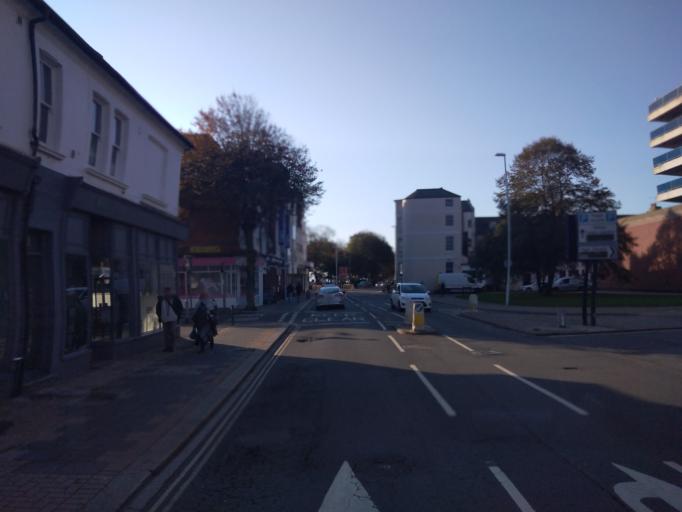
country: GB
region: England
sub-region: West Sussex
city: Worthing
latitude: 50.8129
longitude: -0.3678
